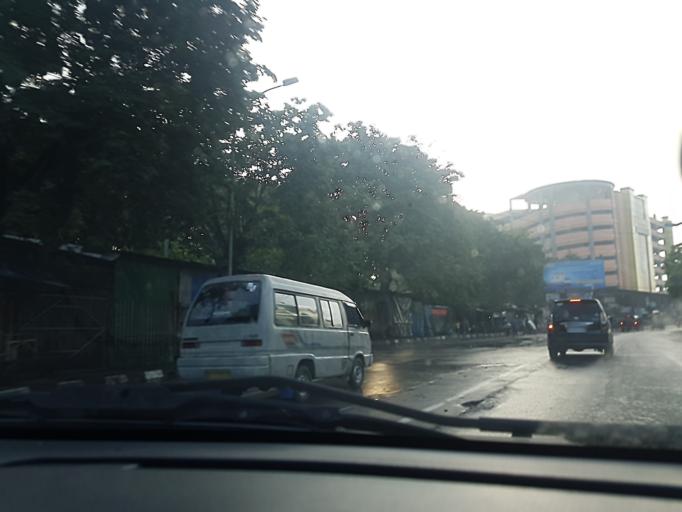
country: ID
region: East Java
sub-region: Kota Surabaya
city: Surabaya
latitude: -7.2456
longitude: 112.7318
